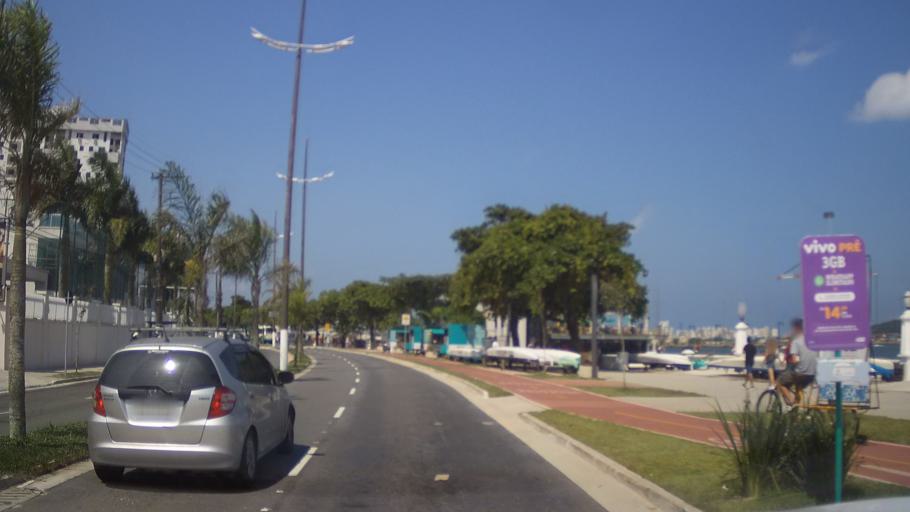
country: BR
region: Sao Paulo
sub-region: Santos
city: Santos
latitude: -23.9914
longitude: -46.3040
